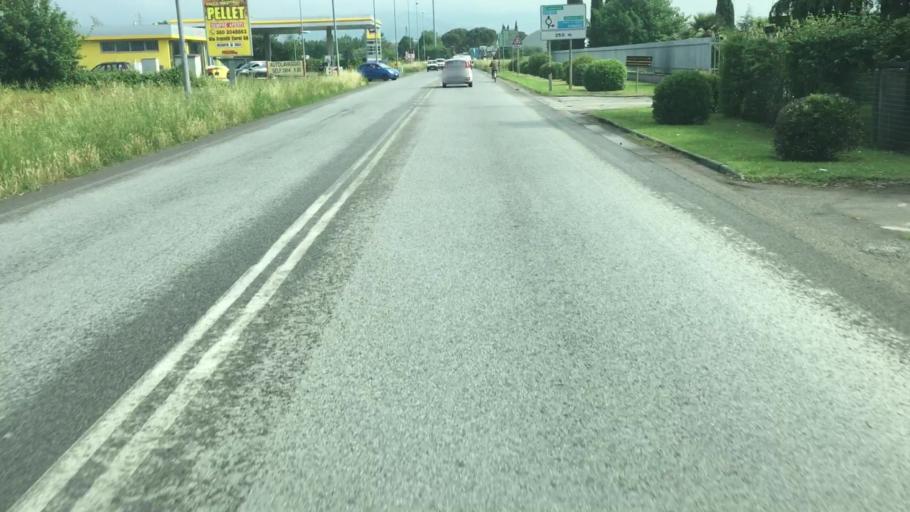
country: IT
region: Tuscany
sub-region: Province of Florence
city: San Mauro
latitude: 43.8133
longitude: 11.1197
